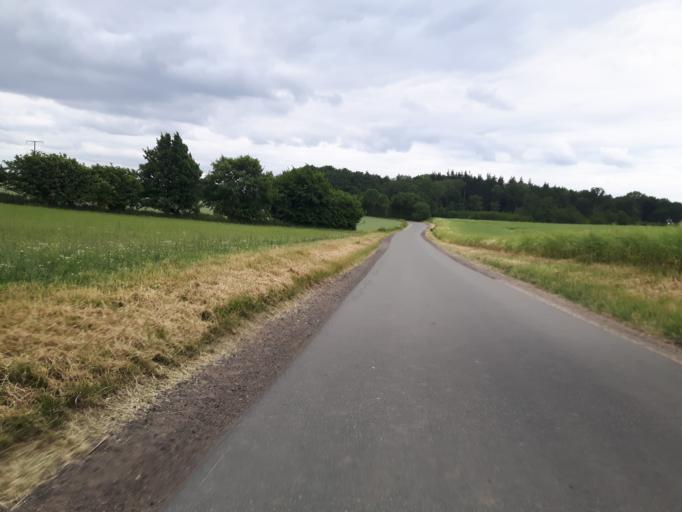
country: DE
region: Schleswig-Holstein
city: Schashagen
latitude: 54.1260
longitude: 10.9075
